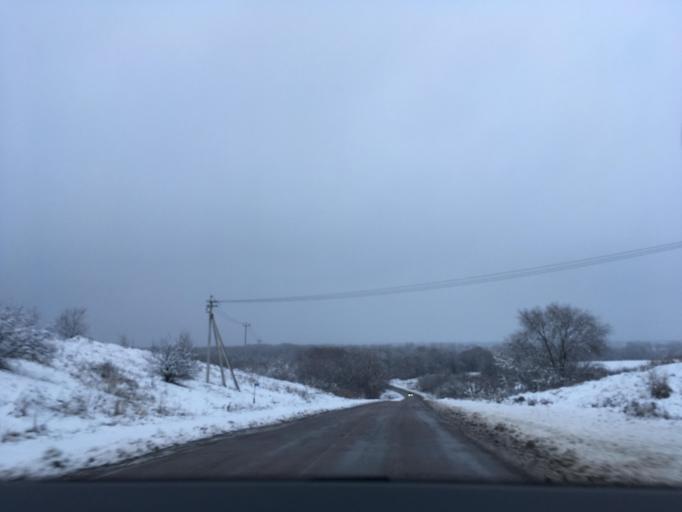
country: RU
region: Voronezj
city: Mitrofanovka
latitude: 50.1351
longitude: 39.9855
